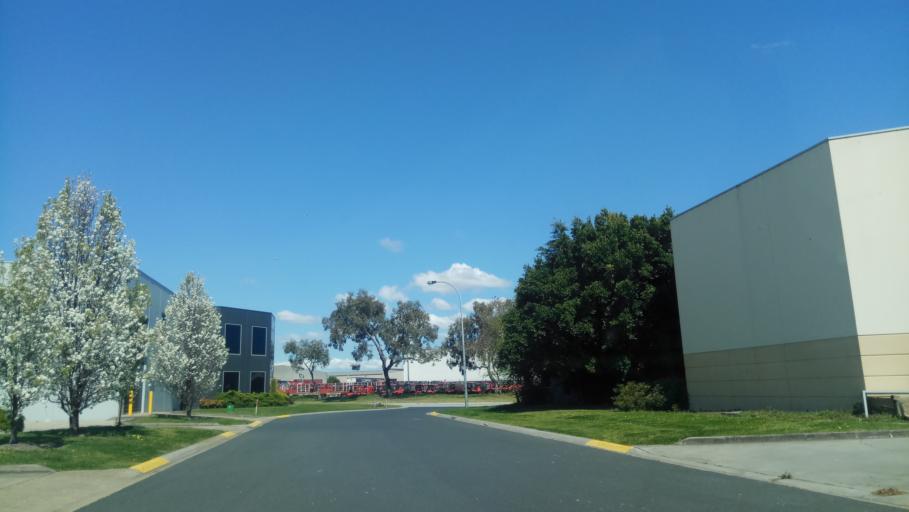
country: AU
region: Victoria
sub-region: Kingston
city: Dingley Village
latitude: -37.9940
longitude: 145.1173
